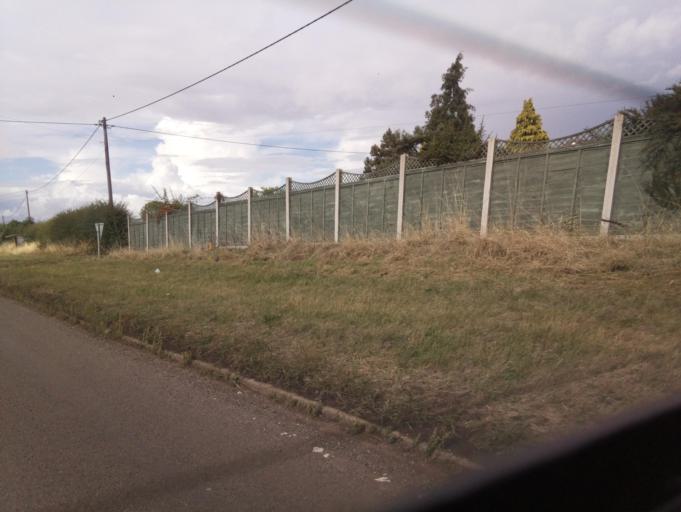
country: GB
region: England
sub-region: Telford and Wrekin
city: Madeley
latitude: 52.6099
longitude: -2.4103
